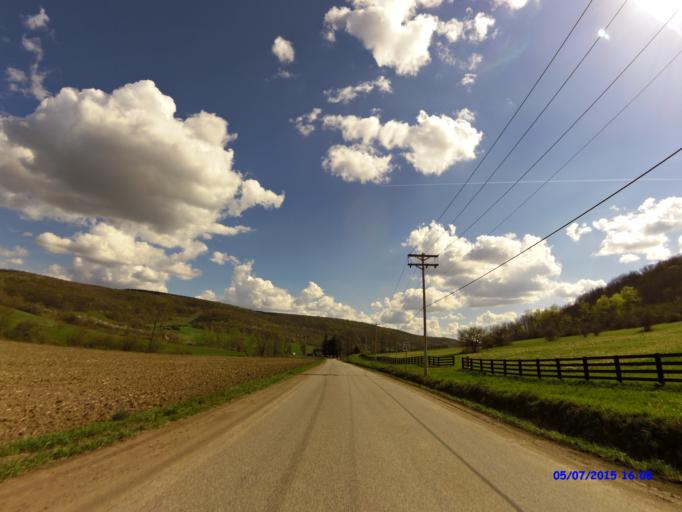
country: US
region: New York
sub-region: Cattaraugus County
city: Franklinville
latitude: 42.2838
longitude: -78.6097
